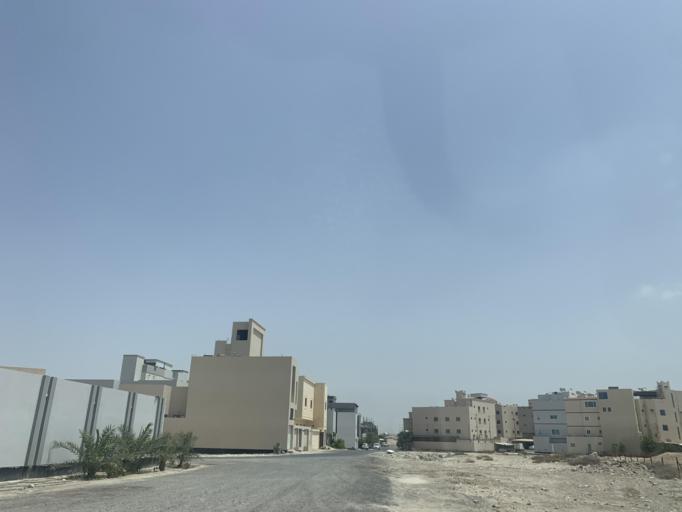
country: BH
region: Central Governorate
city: Madinat Hamad
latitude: 26.1428
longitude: 50.5035
